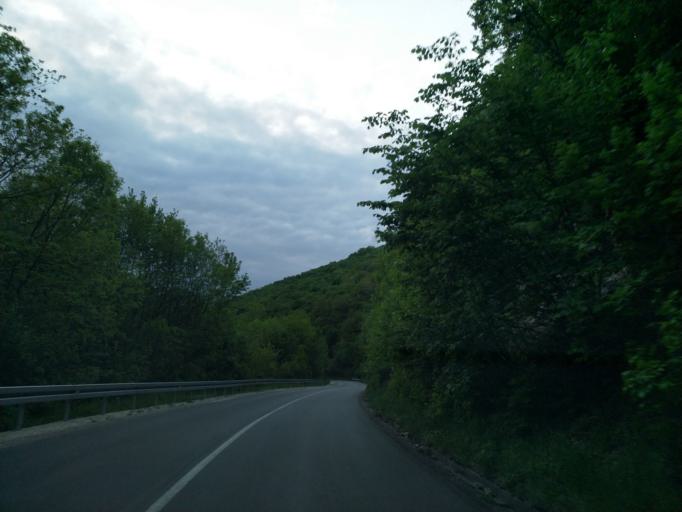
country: RS
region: Central Serbia
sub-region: Pomoravski Okrug
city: Despotovac
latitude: 43.9746
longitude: 21.5120
